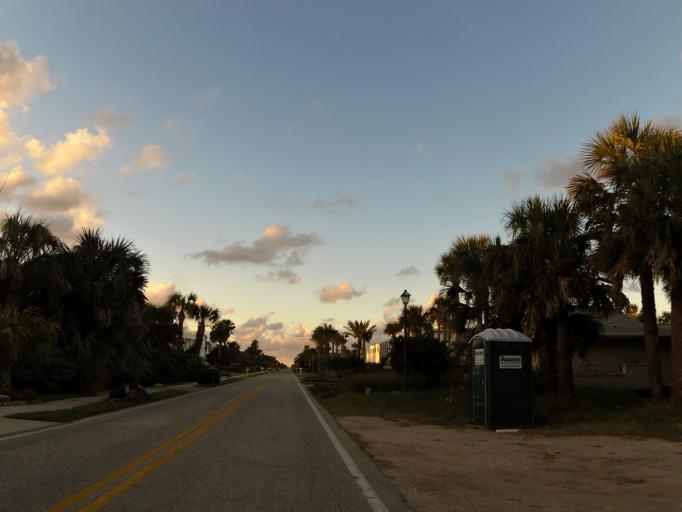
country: US
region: Florida
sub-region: Saint Johns County
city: Sawgrass
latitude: 30.2069
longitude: -81.3689
